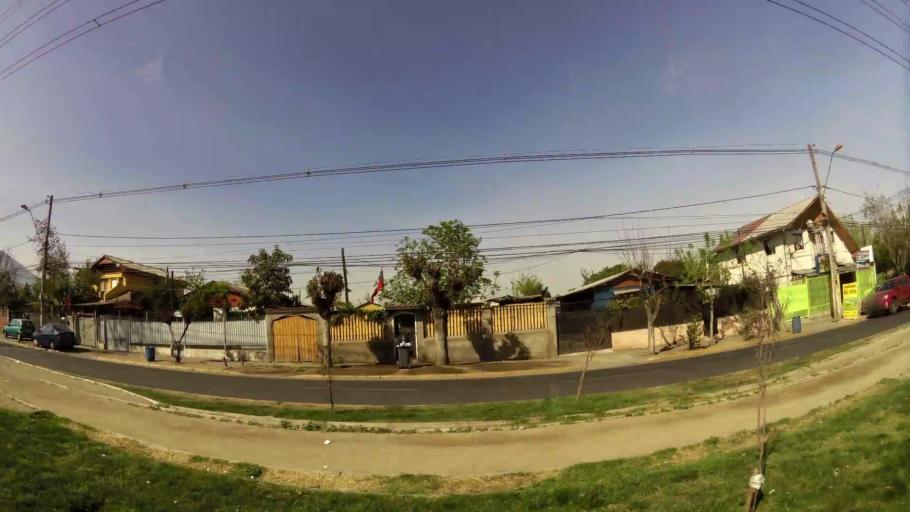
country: CL
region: Santiago Metropolitan
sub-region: Provincia de Santiago
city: Villa Presidente Frei, Nunoa, Santiago, Chile
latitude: -33.5043
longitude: -70.5660
